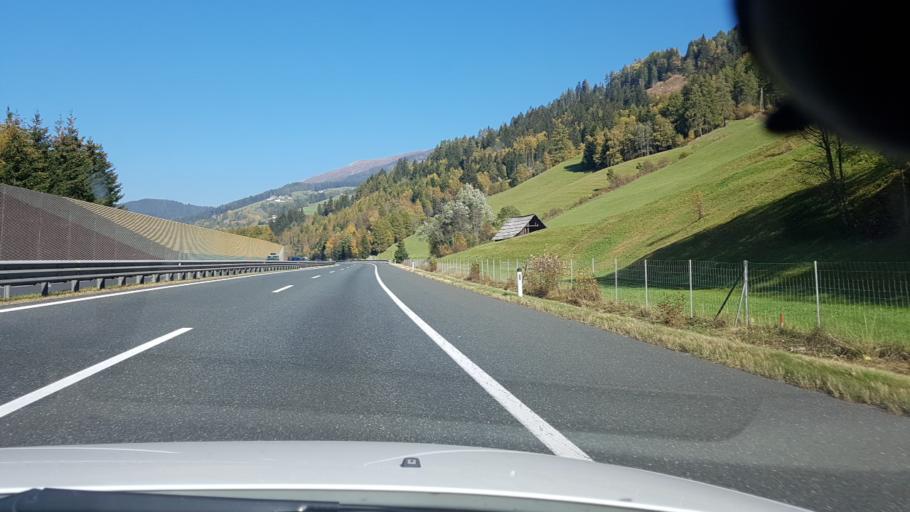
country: AT
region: Salzburg
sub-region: Politischer Bezirk Tamsweg
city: Sankt Michael im Lungau
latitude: 46.9990
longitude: 13.6201
